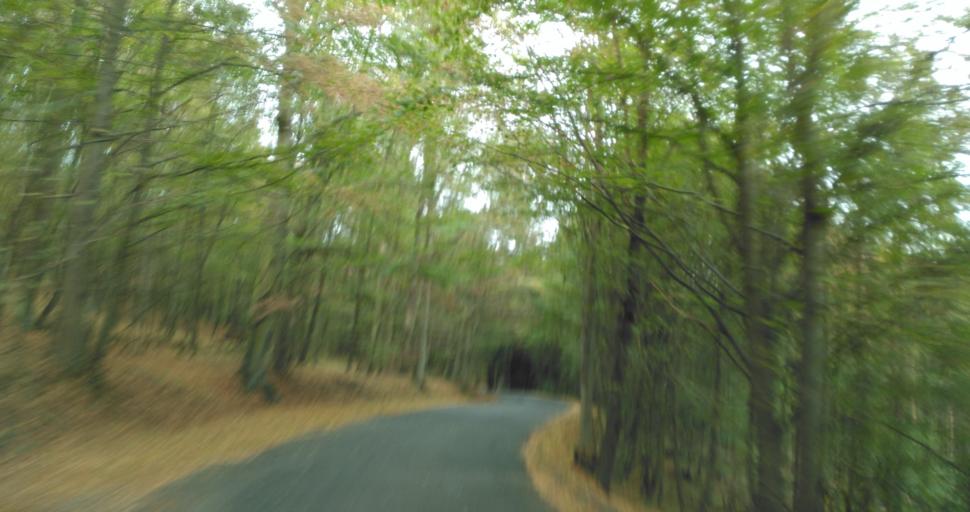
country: CZ
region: Plzensky
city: Zbiroh
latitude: 49.9452
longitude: 13.7688
